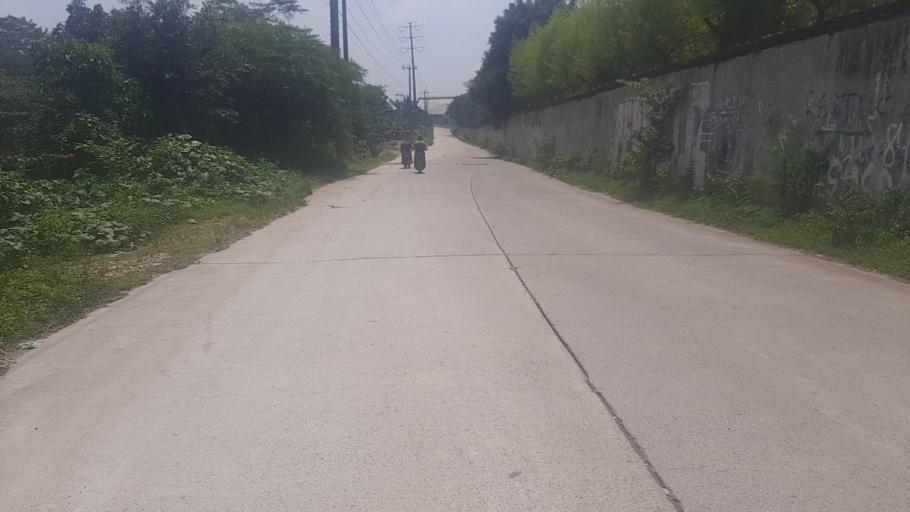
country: ID
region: West Java
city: Citeureup
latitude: -6.4630
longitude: 106.9302
